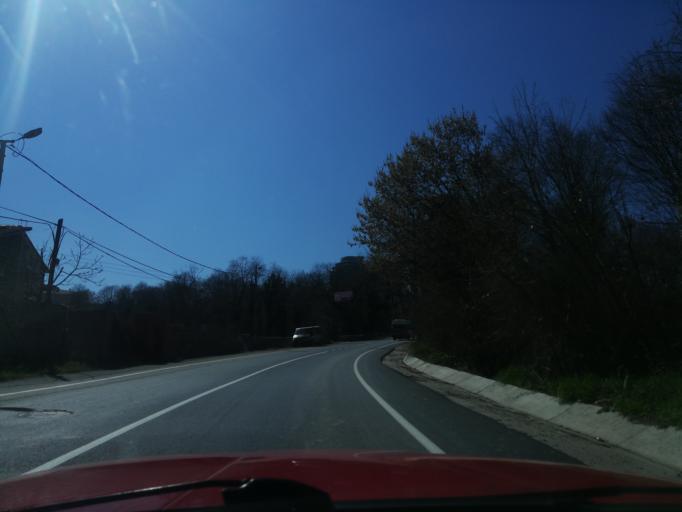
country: TR
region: Istanbul
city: Mahmut Sevket Pasa
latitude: 41.1226
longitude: 29.1518
